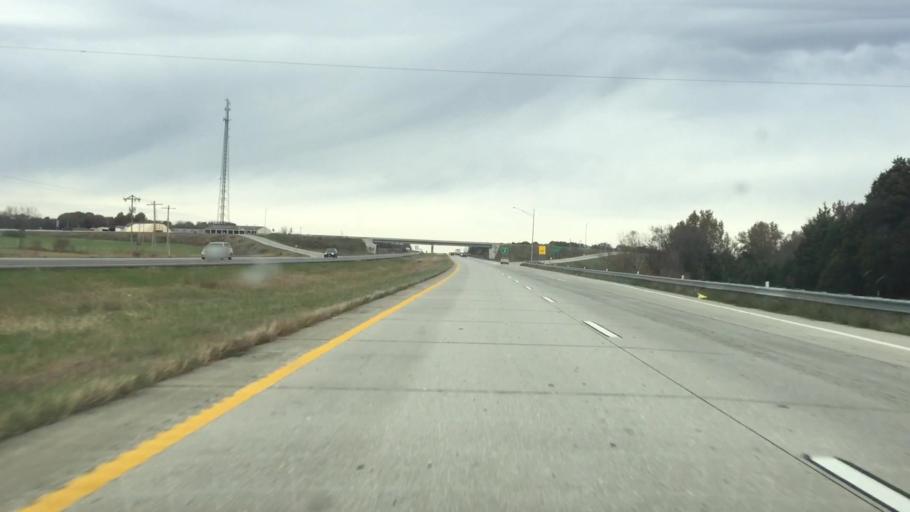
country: US
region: Missouri
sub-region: Saint Clair County
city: Osceola
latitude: 38.0367
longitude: -93.6792
